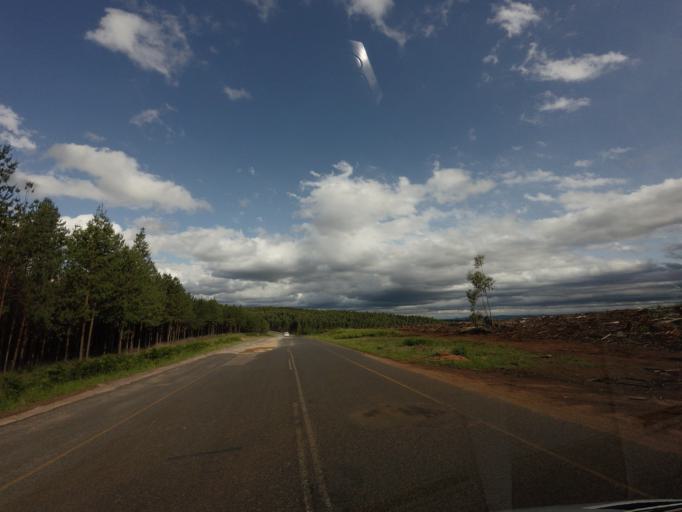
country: ZA
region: Mpumalanga
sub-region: Ehlanzeni District
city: Graksop
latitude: -24.9782
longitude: 30.9488
